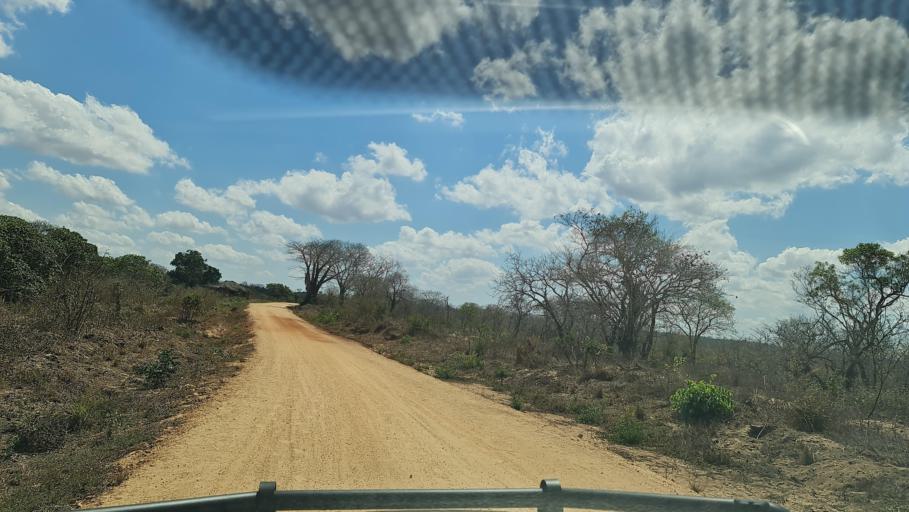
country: MZ
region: Nampula
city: Nacala
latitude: -14.1797
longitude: 40.2232
